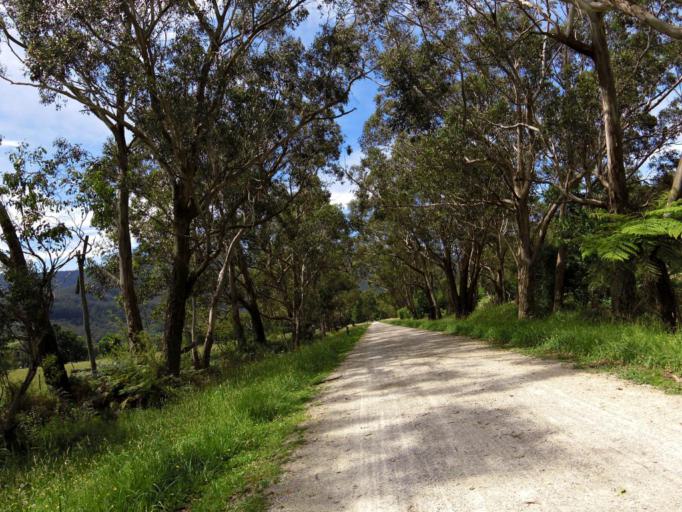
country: AU
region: Victoria
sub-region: Yarra Ranges
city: Millgrove
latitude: -37.7602
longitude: 145.6461
